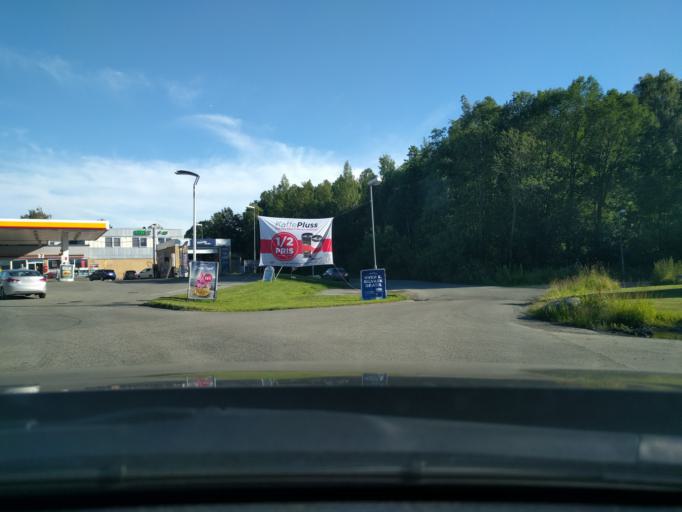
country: NO
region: Buskerud
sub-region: Drammen
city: Skoger
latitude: 59.7496
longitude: 10.2894
